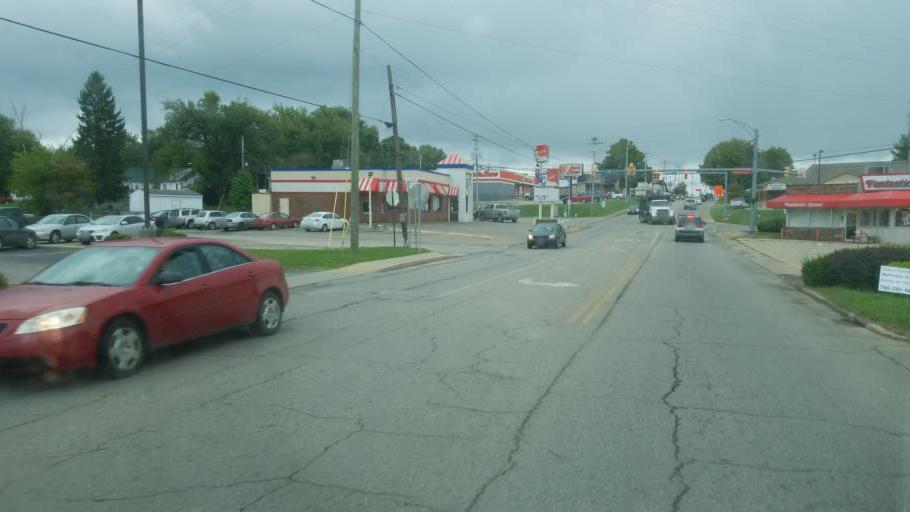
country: US
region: Ohio
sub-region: Jackson County
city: Jackson
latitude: 39.0452
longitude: -82.6304
